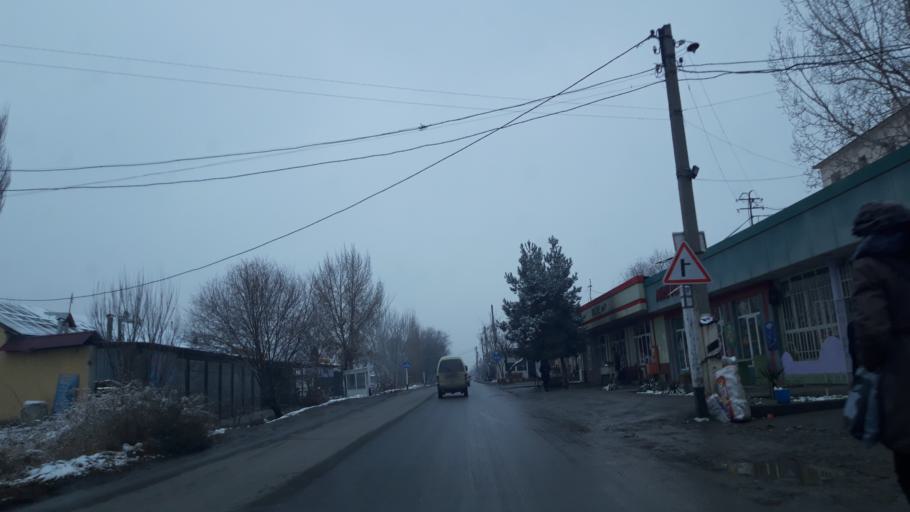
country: UZ
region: Andijon
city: Asaka
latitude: 40.6640
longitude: 72.2401
